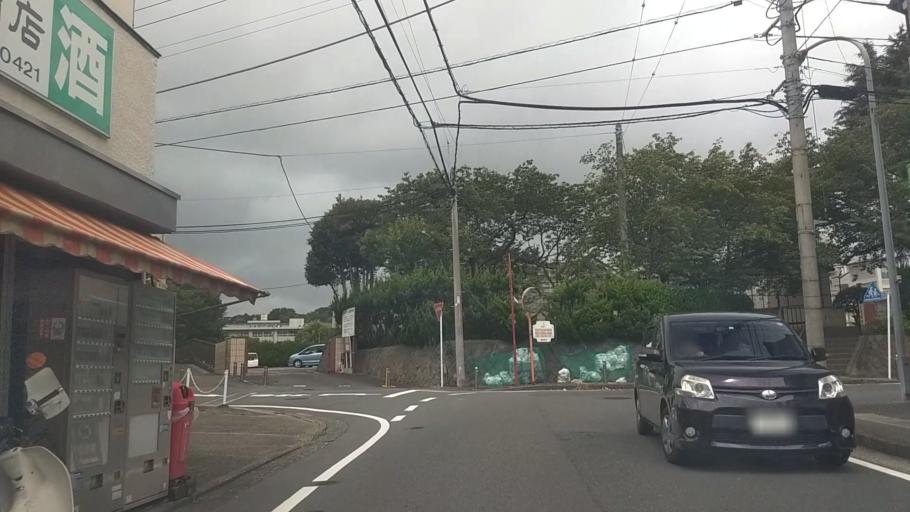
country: JP
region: Kanagawa
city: Yokosuka
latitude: 35.2711
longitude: 139.6609
